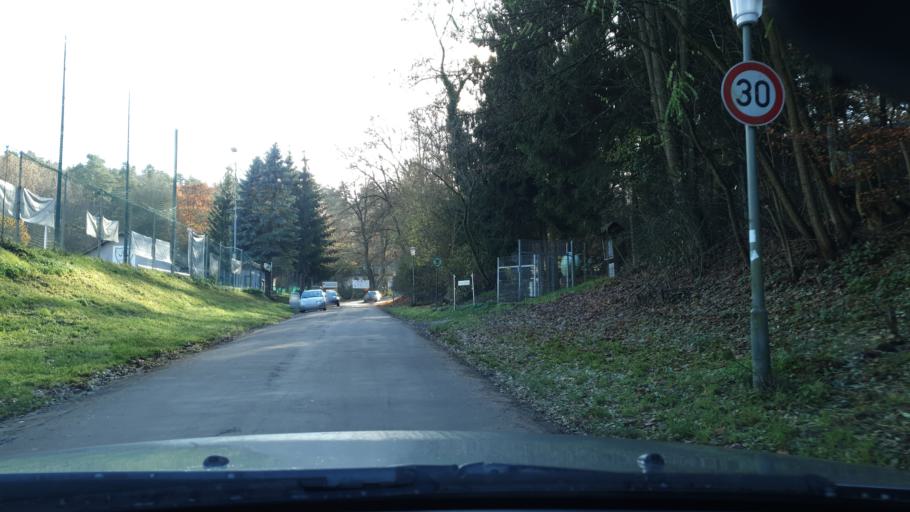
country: DE
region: Rheinland-Pfalz
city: Kaiserslautern
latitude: 49.4396
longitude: 7.7882
